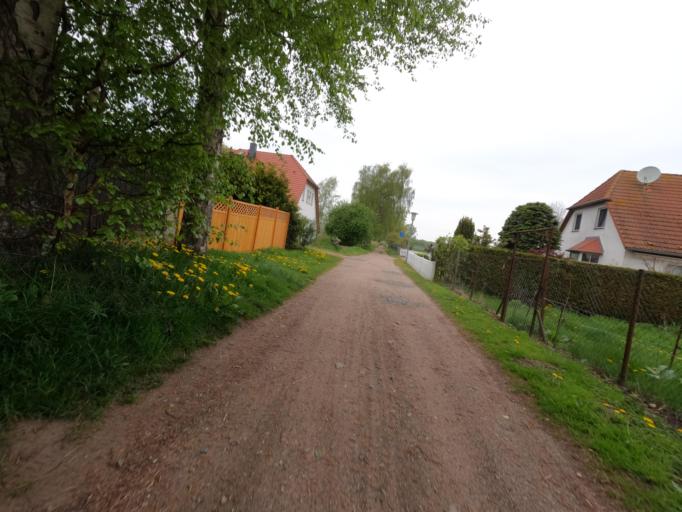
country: DE
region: Mecklenburg-Vorpommern
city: Ostseebad Dierhagen
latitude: 54.2948
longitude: 12.3597
